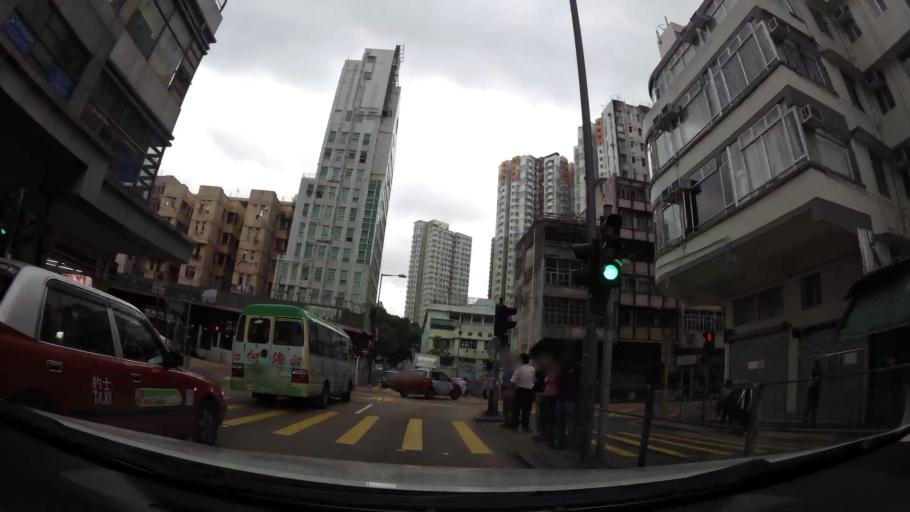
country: HK
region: Kowloon City
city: Kowloon
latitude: 22.3077
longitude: 114.1849
